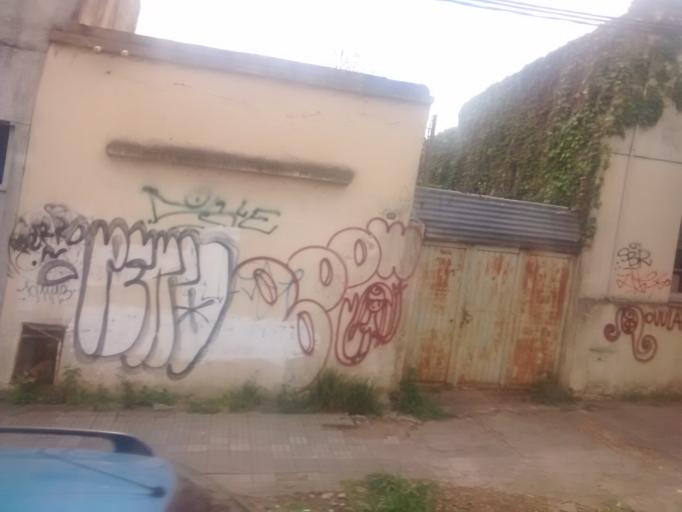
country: AR
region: Buenos Aires
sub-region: Partido de La Plata
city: La Plata
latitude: -34.9290
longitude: -57.9319
